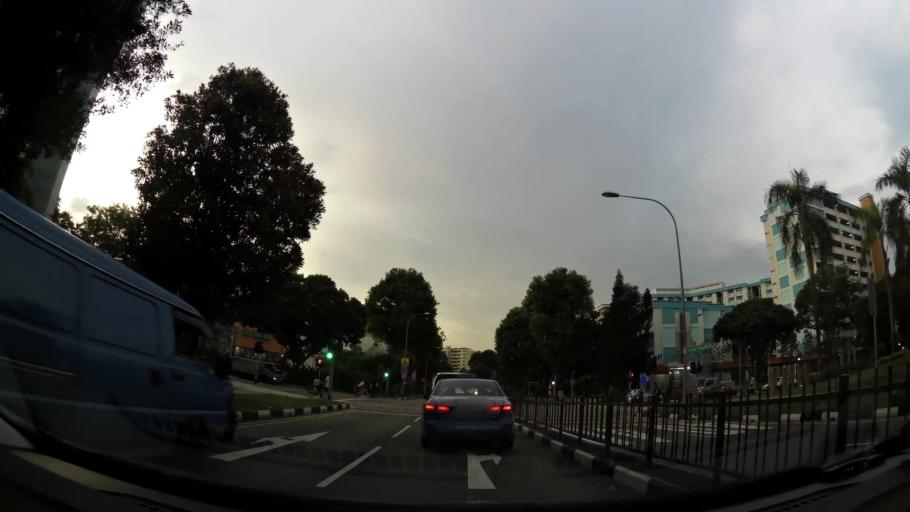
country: MY
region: Johor
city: Kampung Pasir Gudang Baru
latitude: 1.4275
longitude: 103.8316
